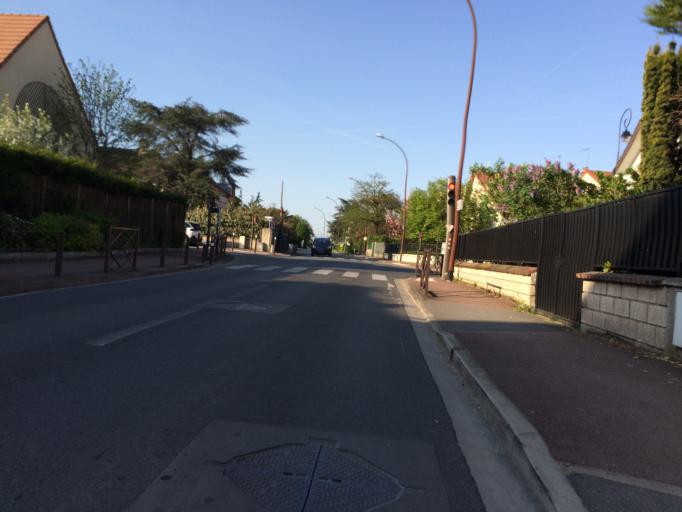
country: FR
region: Ile-de-France
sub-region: Departement des Hauts-de-Seine
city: Chatenay-Malabry
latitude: 48.7575
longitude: 2.2769
